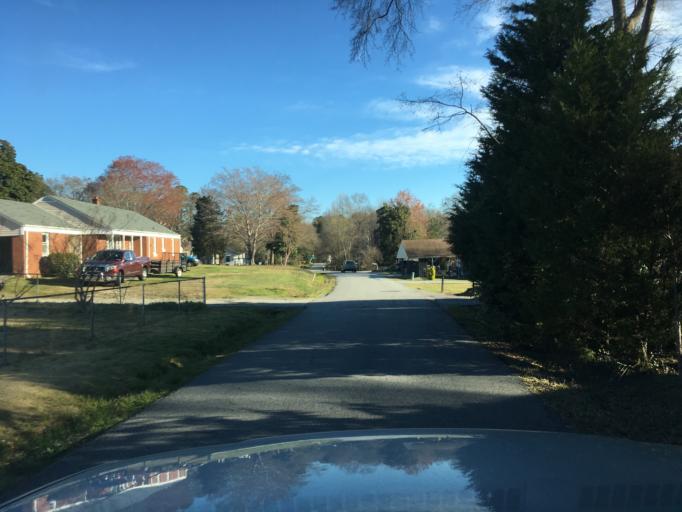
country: US
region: South Carolina
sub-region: Spartanburg County
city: Spartanburg
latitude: 34.9309
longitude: -81.8815
